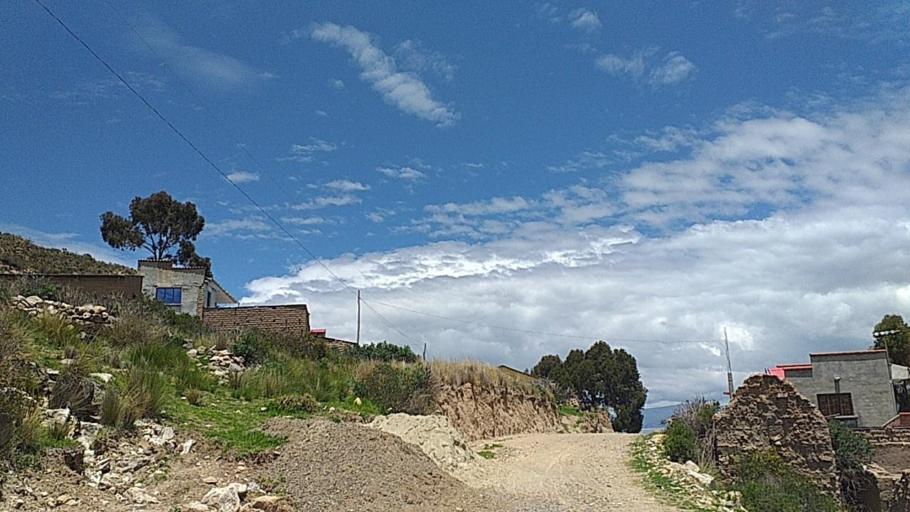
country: BO
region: La Paz
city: Huatajata
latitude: -16.3107
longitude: -68.6792
